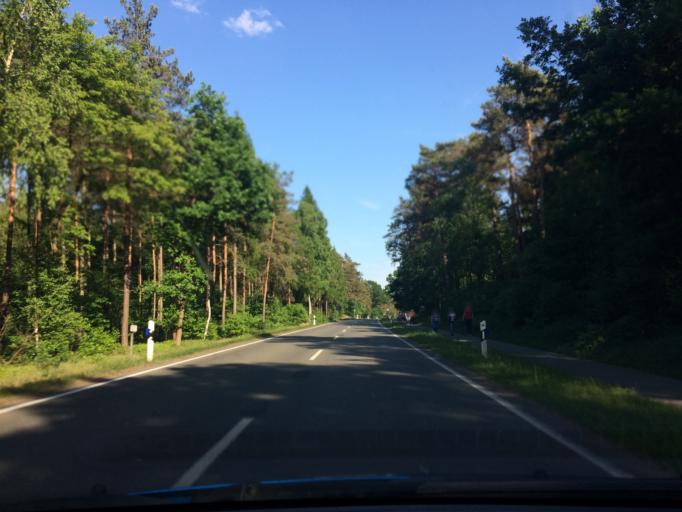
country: DE
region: Lower Saxony
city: Soltau
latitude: 53.0257
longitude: 9.8598
